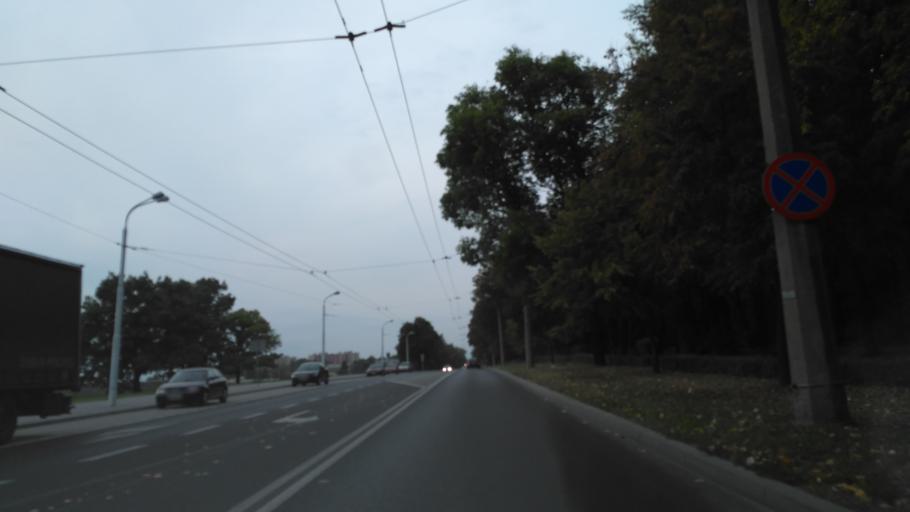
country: PL
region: Lublin Voivodeship
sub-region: Powiat lubelski
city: Lublin
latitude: 51.2256
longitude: 22.6071
